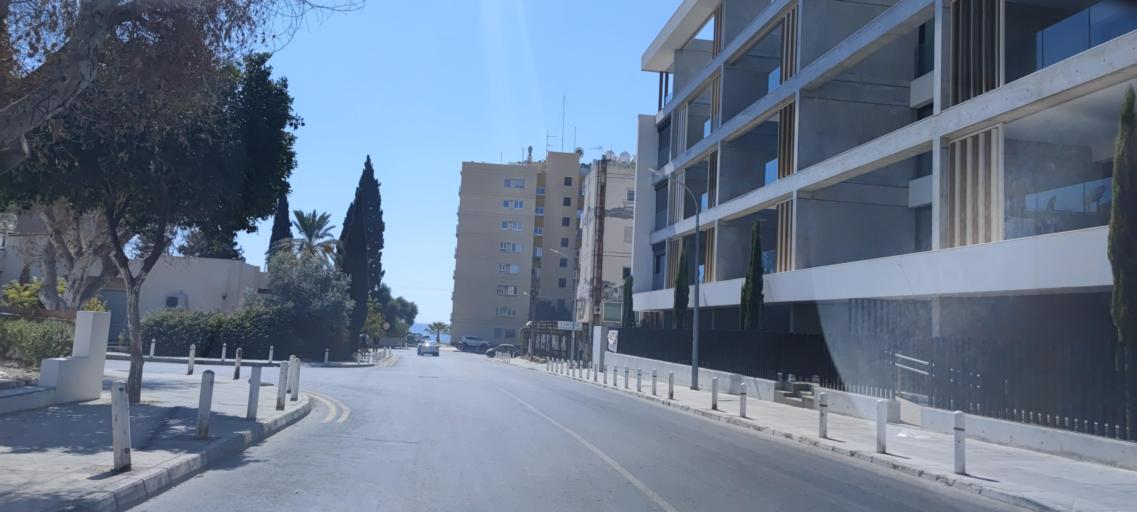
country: CY
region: Limassol
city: Mouttagiaka
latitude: 34.7002
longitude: 33.0991
